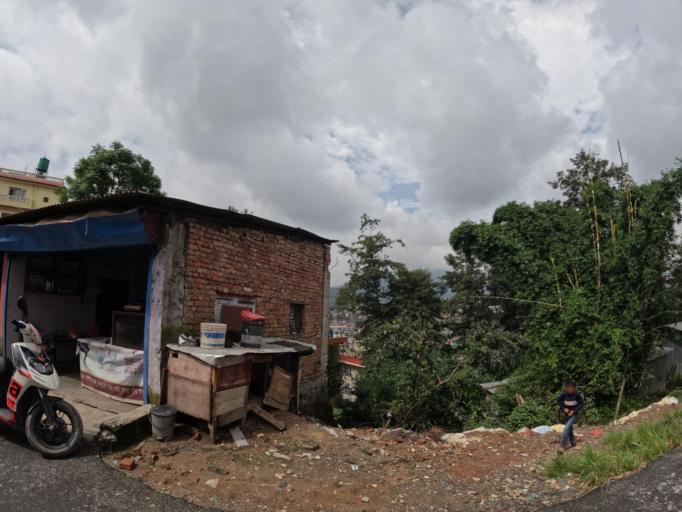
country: NP
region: Central Region
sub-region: Bagmati Zone
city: Kathmandu
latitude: 27.7509
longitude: 85.3202
